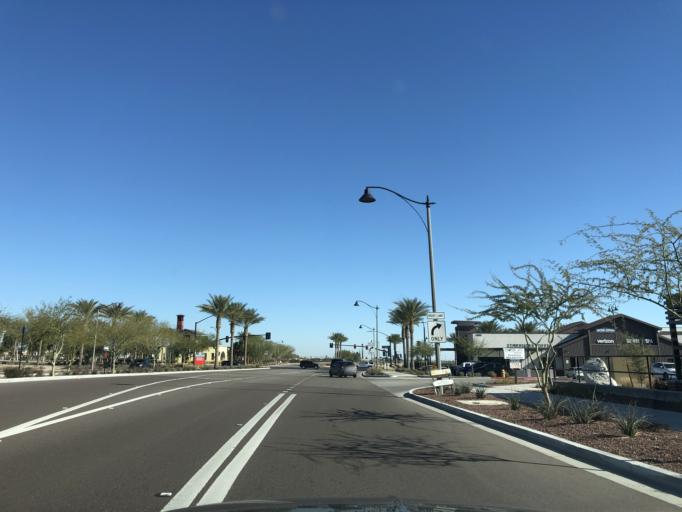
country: US
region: Arizona
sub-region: Maricopa County
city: Citrus Park
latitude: 33.4668
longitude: -112.5059
